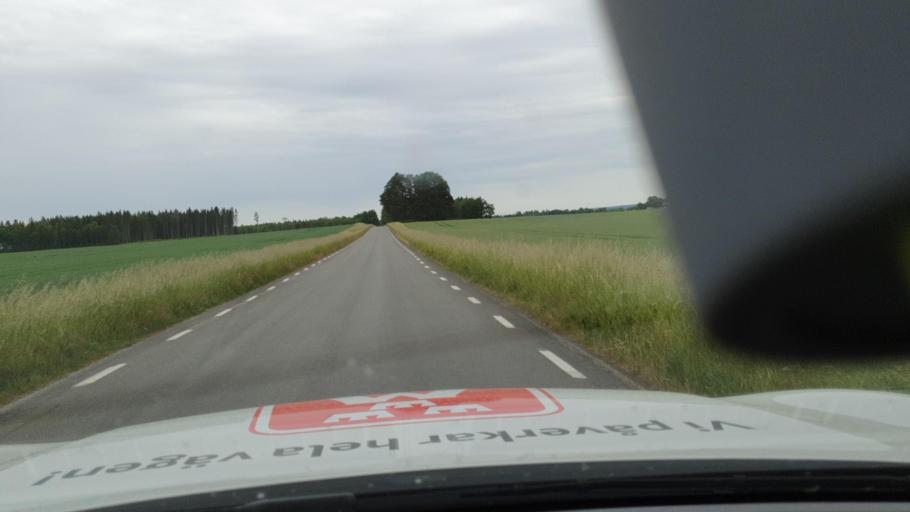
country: SE
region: Vaestra Goetaland
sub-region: Tibro Kommun
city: Tibro
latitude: 58.3332
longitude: 14.1008
